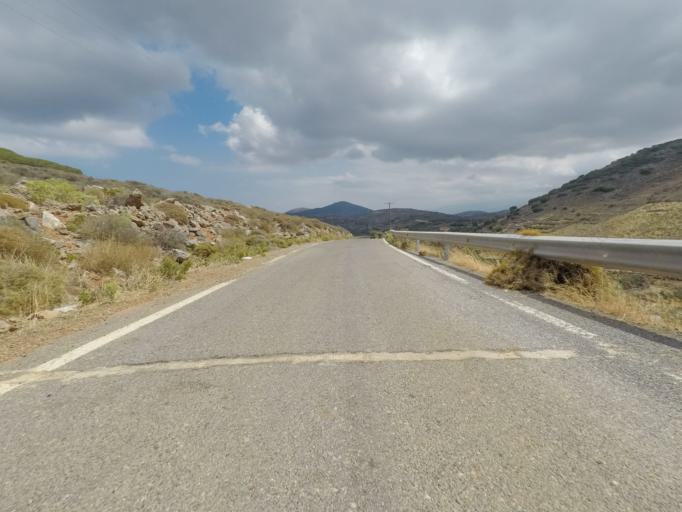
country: GR
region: Crete
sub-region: Nomos Lasithiou
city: Elounda
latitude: 35.2983
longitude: 25.6743
